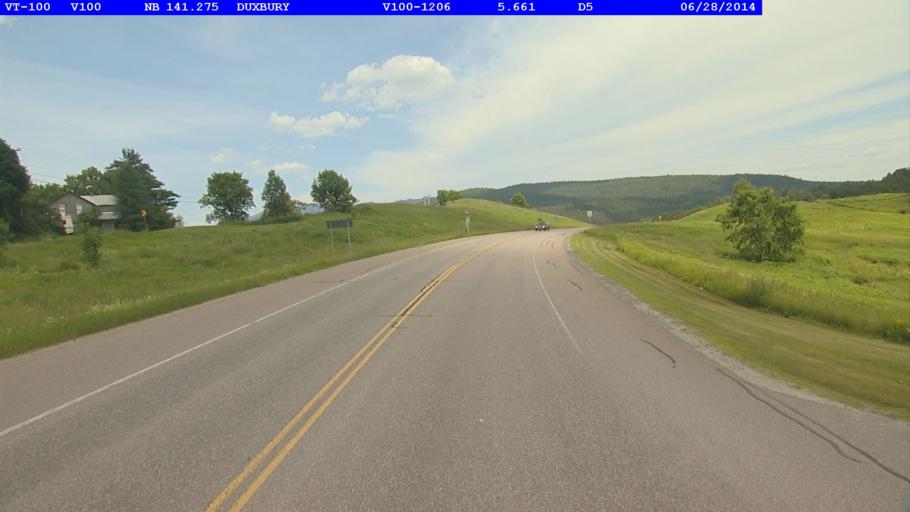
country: US
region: Vermont
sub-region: Washington County
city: Waterbury
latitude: 44.3225
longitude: -72.7563
